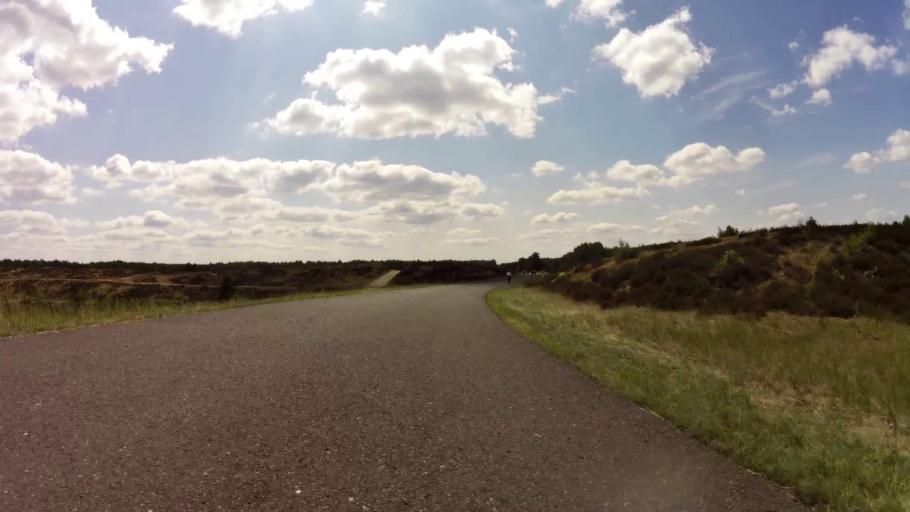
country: PL
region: West Pomeranian Voivodeship
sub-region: Powiat drawski
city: Drawsko Pomorskie
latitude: 53.4132
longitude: 15.7382
